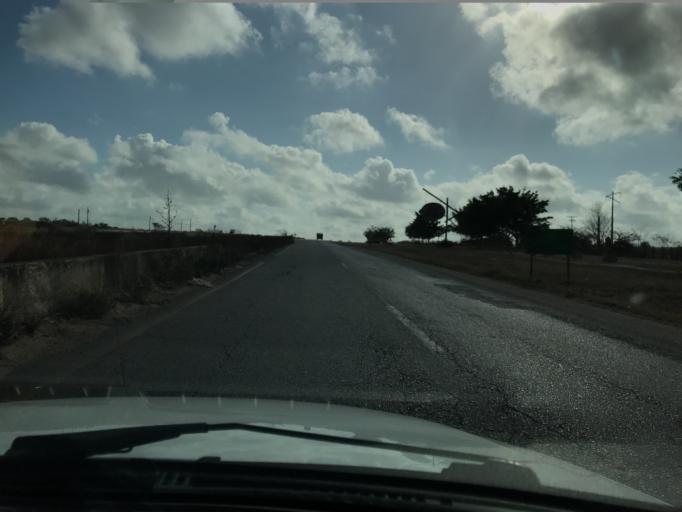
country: BR
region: Pernambuco
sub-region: Bezerros
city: Bezerros
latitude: -8.2288
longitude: -35.7019
